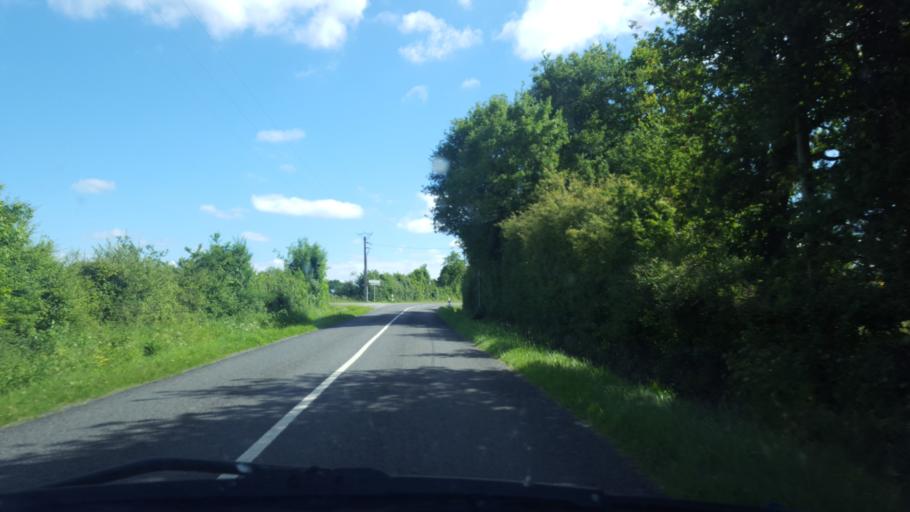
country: FR
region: Pays de la Loire
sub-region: Departement de la Loire-Atlantique
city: Paulx
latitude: 47.0052
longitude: -1.7338
